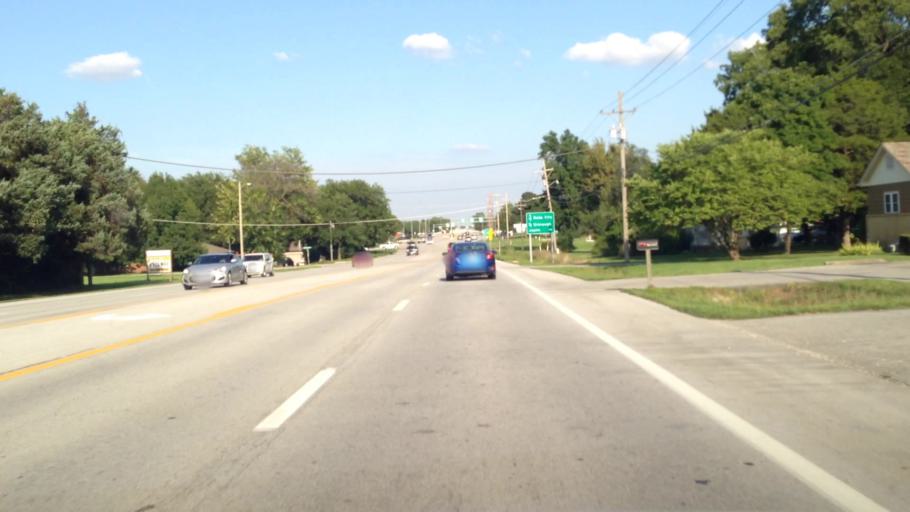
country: US
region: Missouri
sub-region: Jasper County
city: Webb City
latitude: 37.1428
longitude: -94.5165
